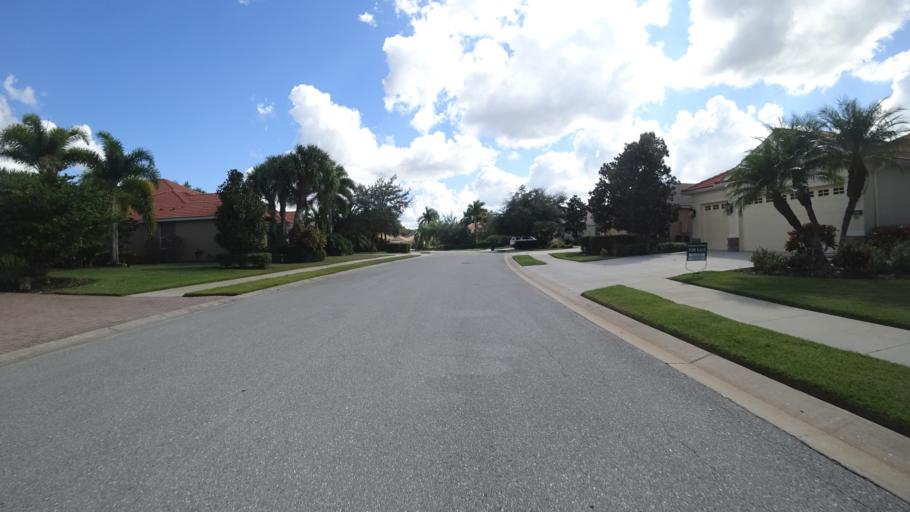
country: US
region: Florida
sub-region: Sarasota County
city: The Meadows
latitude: 27.4229
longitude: -82.3906
